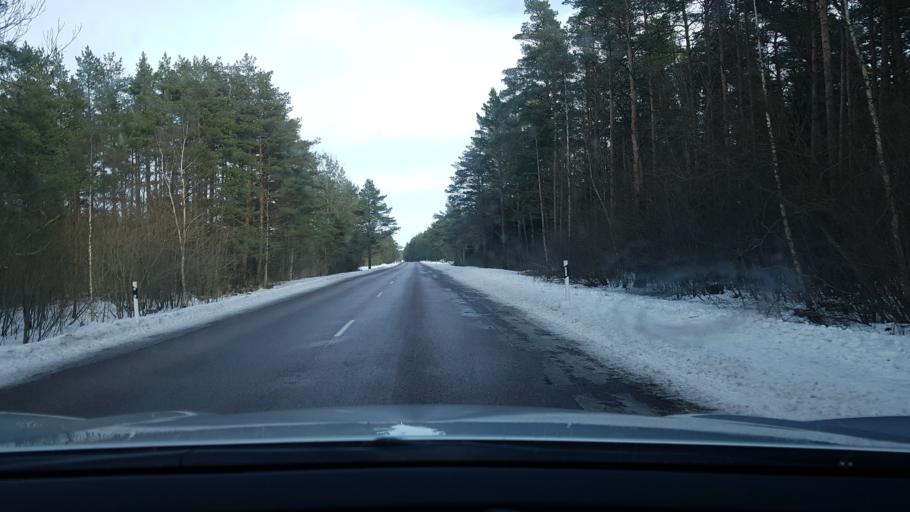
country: EE
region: Saare
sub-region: Kuressaare linn
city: Kuressaare
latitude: 58.3413
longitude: 22.5773
